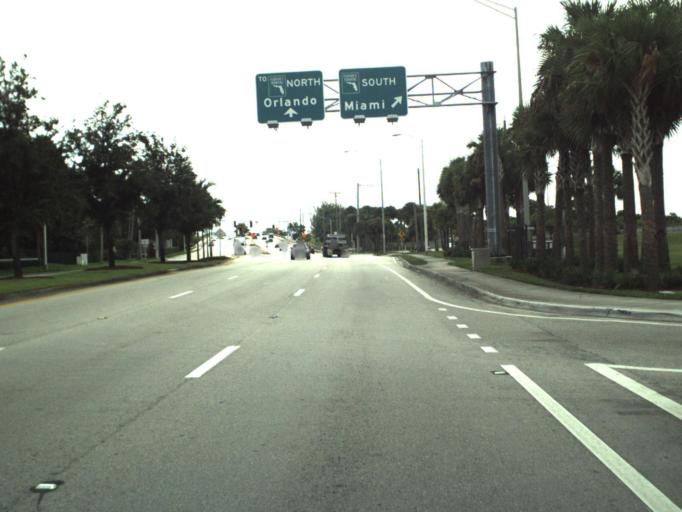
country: US
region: Florida
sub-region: Broward County
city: Coconut Creek
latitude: 26.2316
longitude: -80.1836
